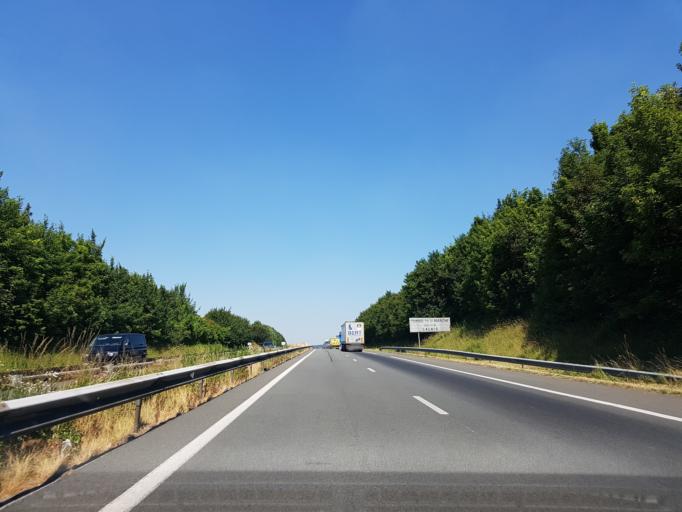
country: FR
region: Nord-Pas-de-Calais
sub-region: Departement du Nord
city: Marcoing
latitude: 50.1223
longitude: 3.1543
